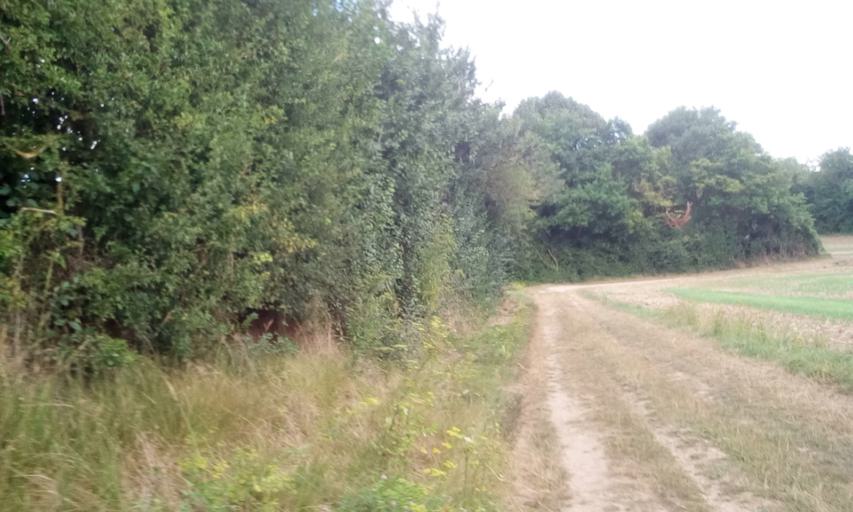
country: FR
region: Lower Normandy
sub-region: Departement du Calvados
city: Bellengreville
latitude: 49.1136
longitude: -0.1977
